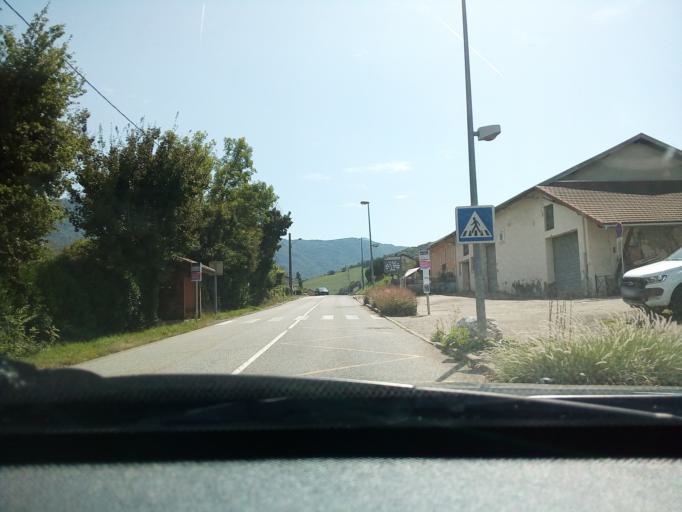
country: FR
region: Rhone-Alpes
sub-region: Departement de l'Isere
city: Brie-et-Angonnes
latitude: 45.1155
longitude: 5.7839
